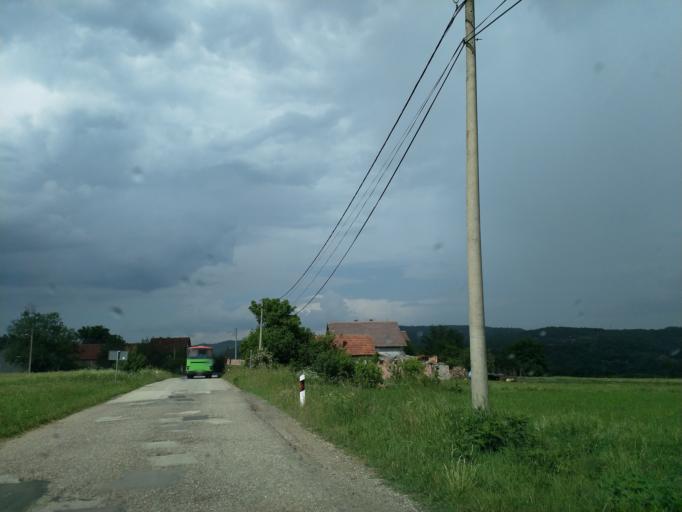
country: RS
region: Central Serbia
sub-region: Borski Okrug
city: Bor
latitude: 44.0027
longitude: 21.9803
